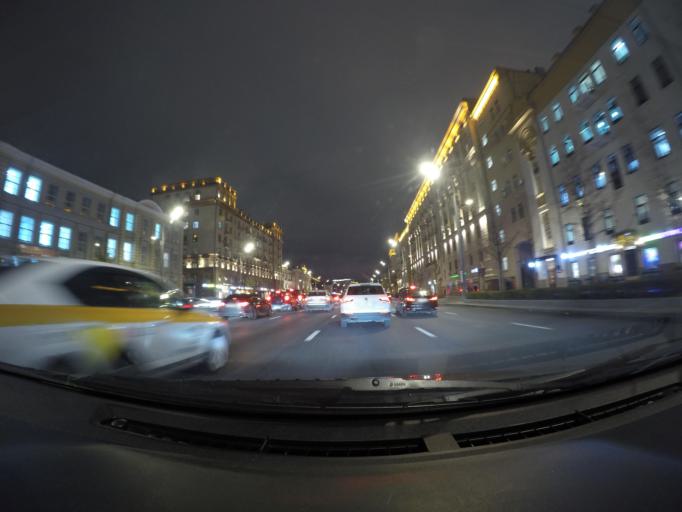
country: RU
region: Moskovskaya
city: Dorogomilovo
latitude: 55.7604
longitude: 37.5857
